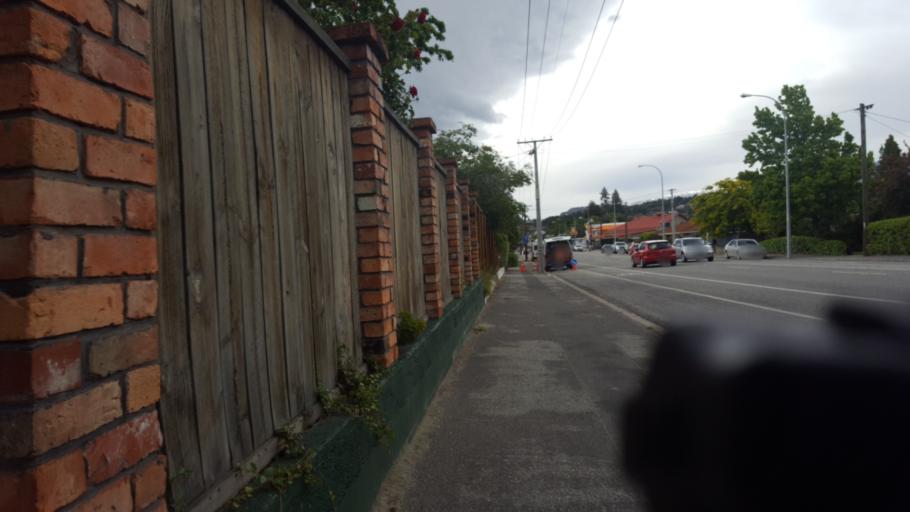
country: NZ
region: Otago
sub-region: Queenstown-Lakes District
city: Wanaka
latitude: -45.2513
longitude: 169.3961
